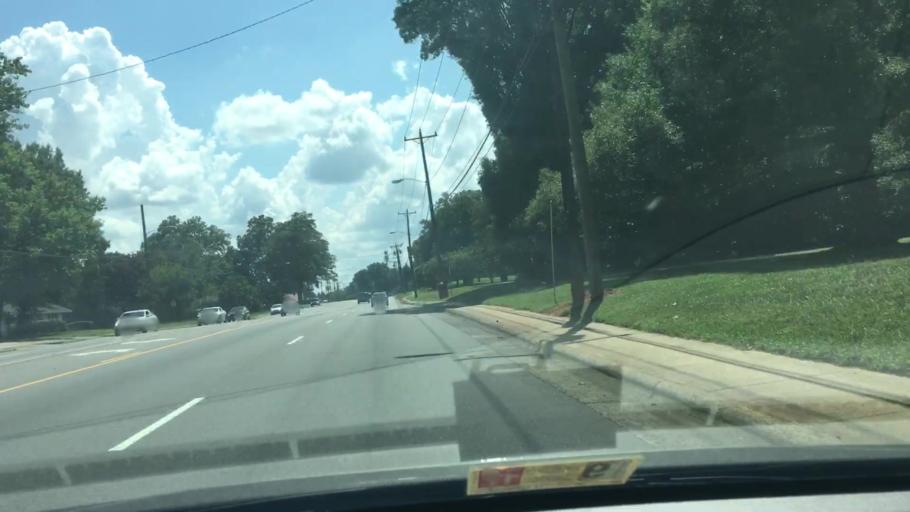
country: US
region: North Carolina
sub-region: Mecklenburg County
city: Charlotte
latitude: 35.2707
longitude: -80.7943
